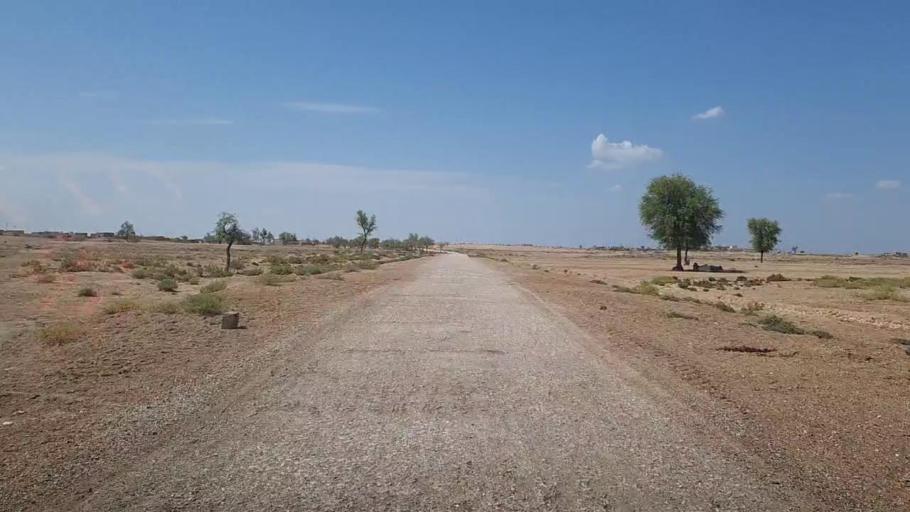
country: PK
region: Sindh
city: Sehwan
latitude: 26.3477
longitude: 67.6739
